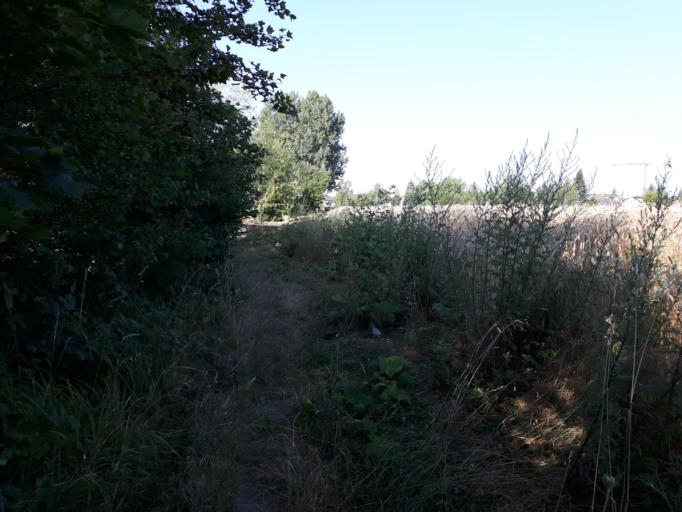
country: DE
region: Baden-Wuerttemberg
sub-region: Karlsruhe Region
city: Karlsdorf-Neuthard
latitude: 49.1018
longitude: 8.5379
